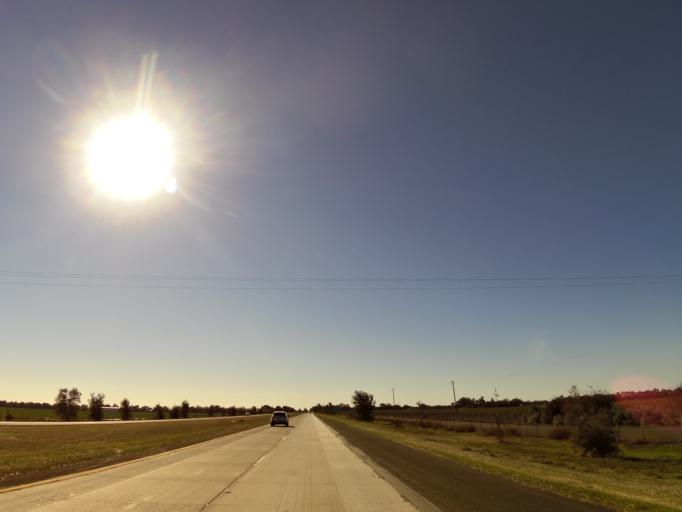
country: US
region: California
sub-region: Yolo County
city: Woodland
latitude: 38.6123
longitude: -121.7670
